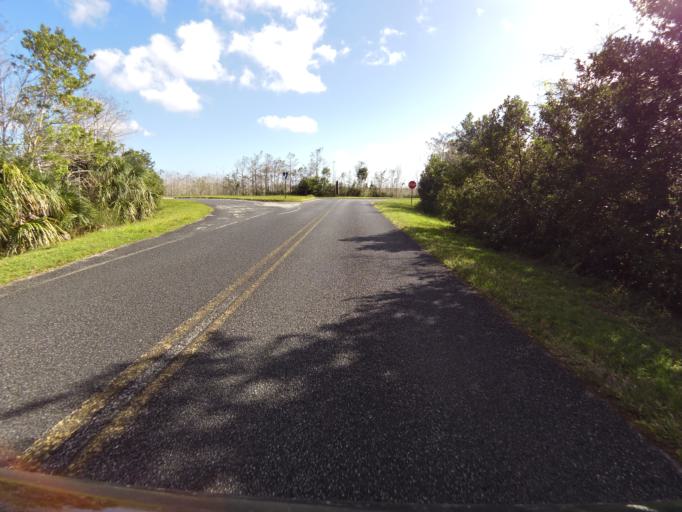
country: US
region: Florida
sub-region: Miami-Dade County
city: Florida City
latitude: 25.4282
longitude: -80.7712
